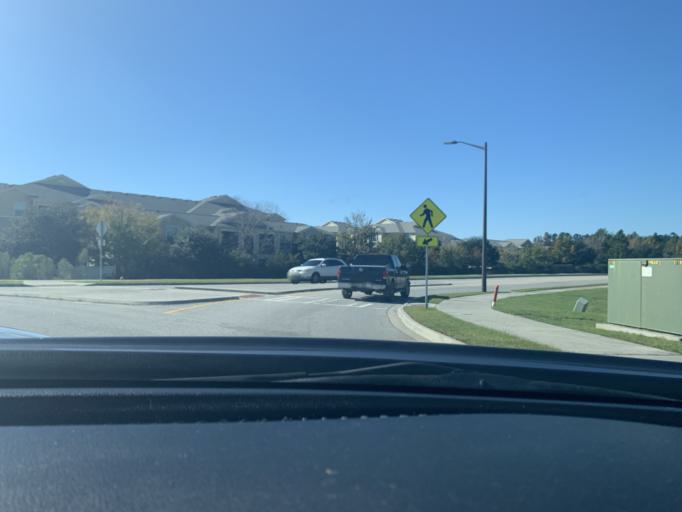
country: US
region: Georgia
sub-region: Chatham County
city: Pooler
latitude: 32.1323
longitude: -81.2484
